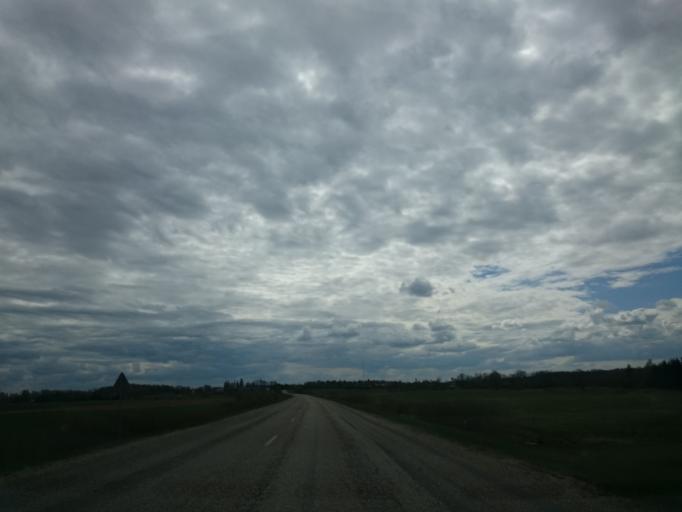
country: LV
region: Aizpute
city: Aizpute
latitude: 56.7507
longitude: 21.6130
